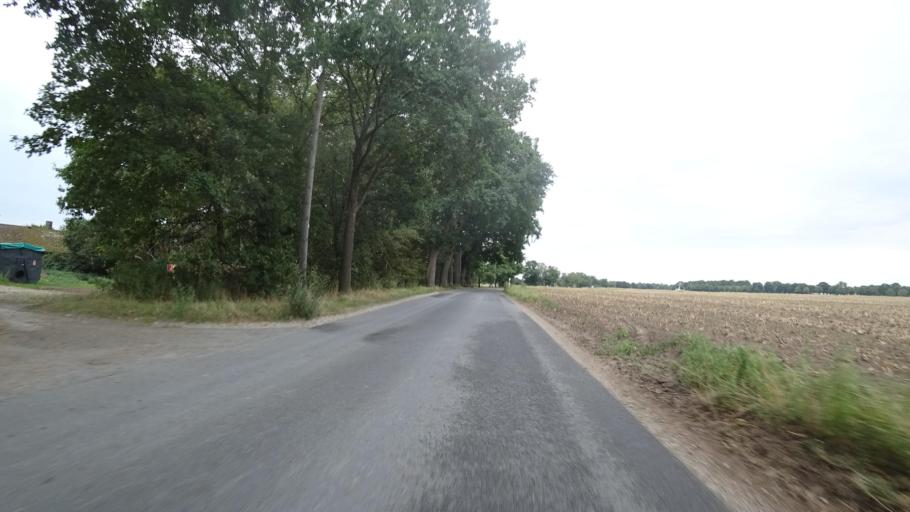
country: DE
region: North Rhine-Westphalia
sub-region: Regierungsbezirk Detmold
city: Rheda-Wiedenbruck
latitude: 51.8760
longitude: 8.2968
